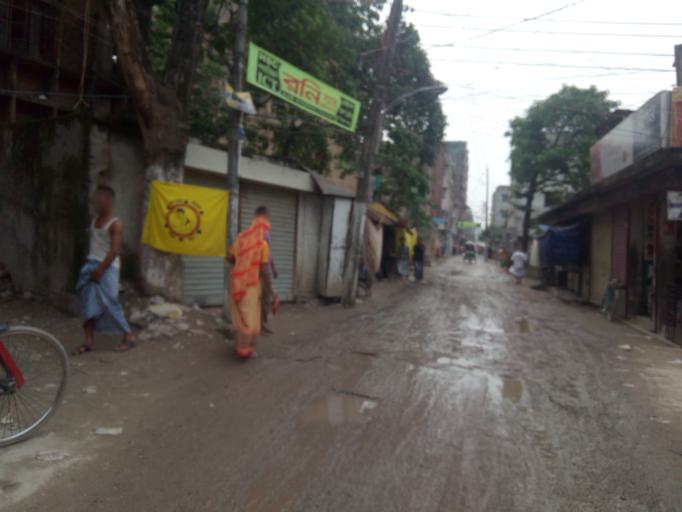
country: BD
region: Dhaka
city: Paltan
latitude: 23.7542
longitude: 90.4307
